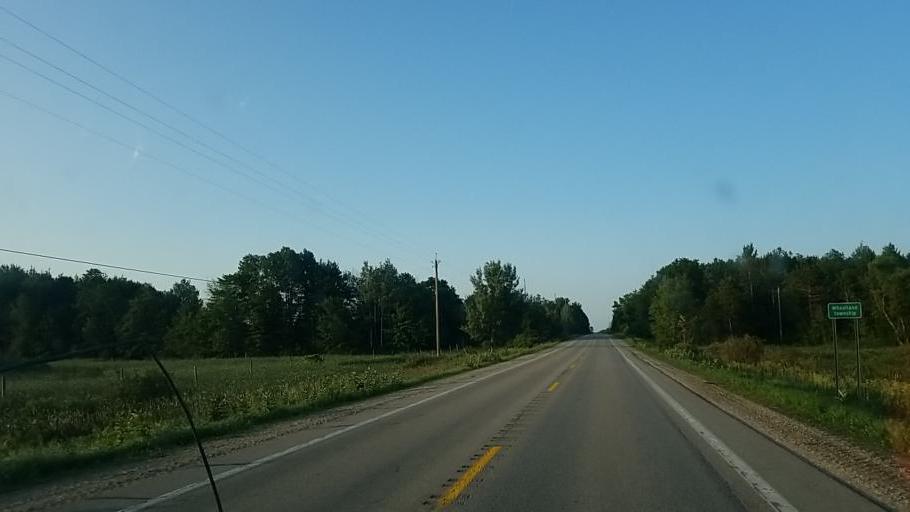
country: US
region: Michigan
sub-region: Isabella County
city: Lake Isabella
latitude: 43.6380
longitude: -85.1461
